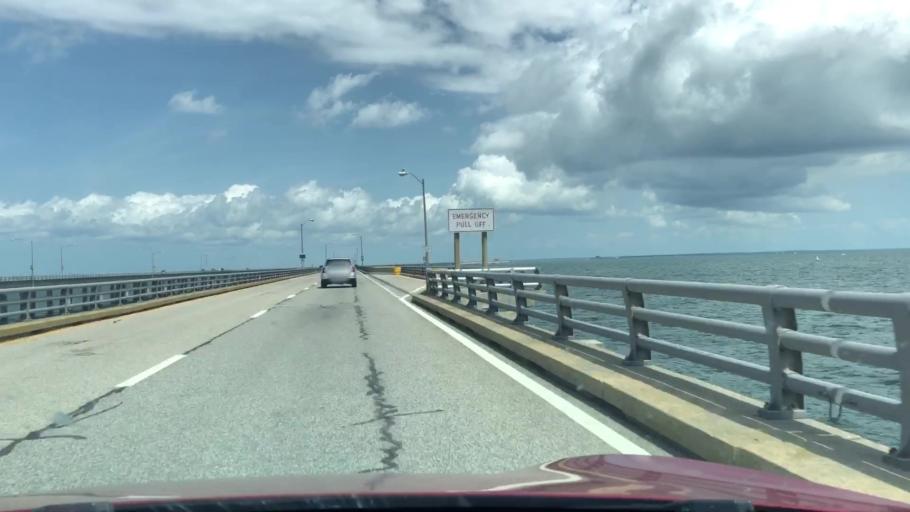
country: US
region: Virginia
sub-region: City of Virginia Beach
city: Virginia Beach
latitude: 37.0093
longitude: -76.0949
